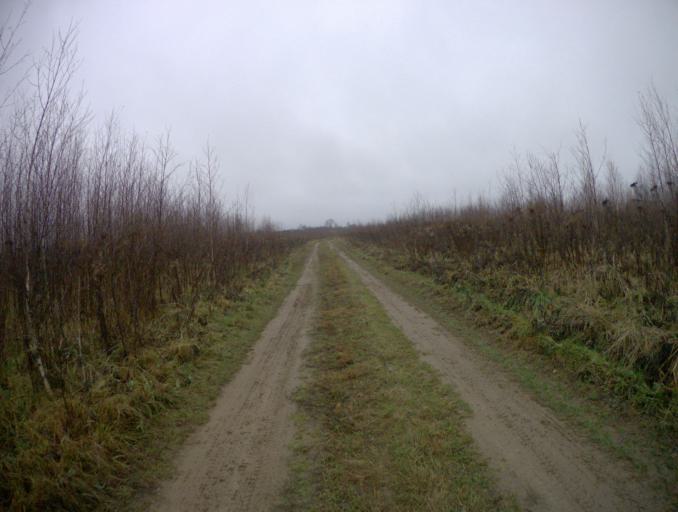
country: RU
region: Vladimir
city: Golovino
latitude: 55.9865
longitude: 40.4468
